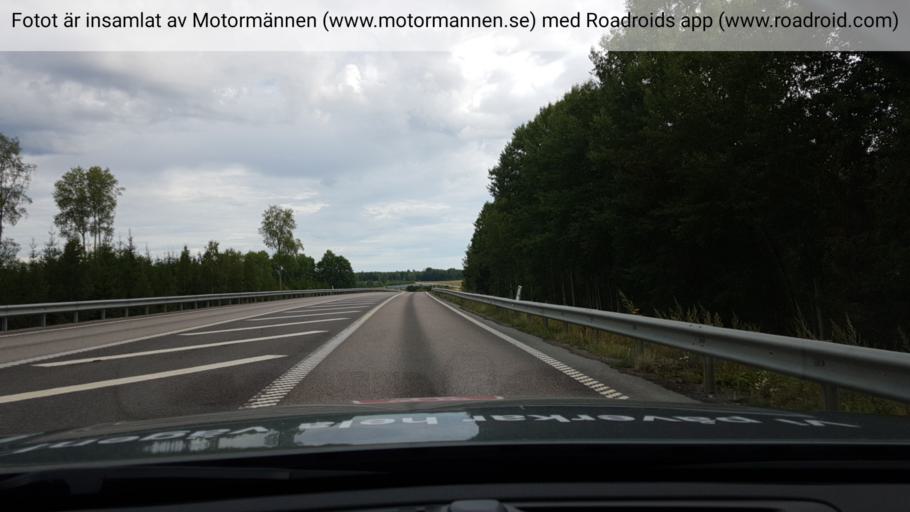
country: SE
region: Uppsala
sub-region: Heby Kommun
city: Heby
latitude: 59.9455
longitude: 16.8312
